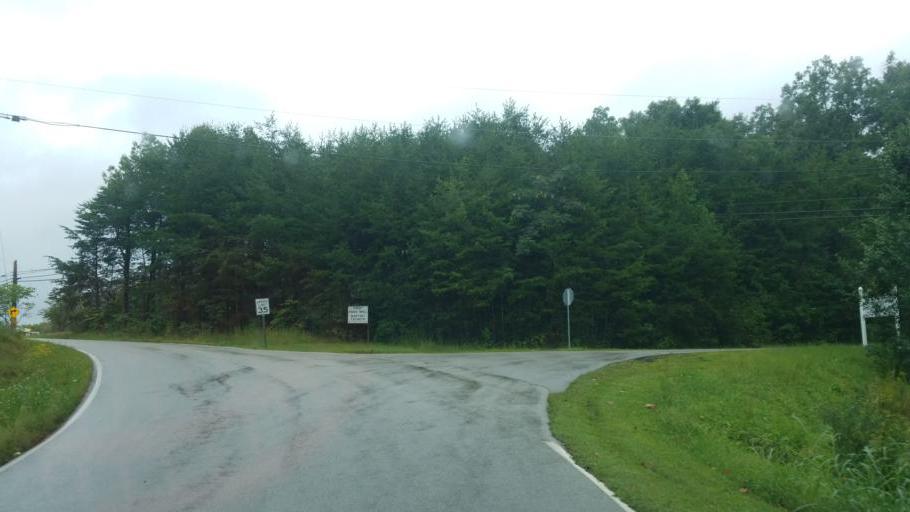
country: US
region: Kentucky
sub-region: Rowan County
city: Morehead
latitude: 38.1502
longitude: -83.5073
